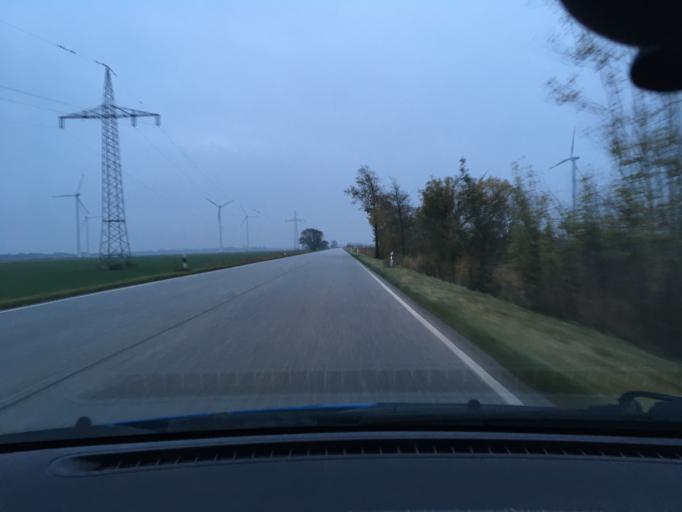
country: DE
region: Schleswig-Holstein
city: Hemme
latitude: 54.2672
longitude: 9.0242
